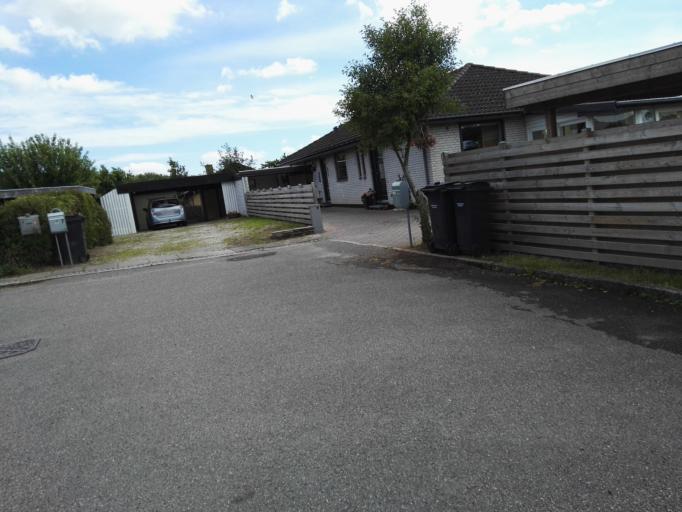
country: DK
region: Capital Region
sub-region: Frederikssund Kommune
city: Slangerup
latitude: 55.8438
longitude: 12.1869
